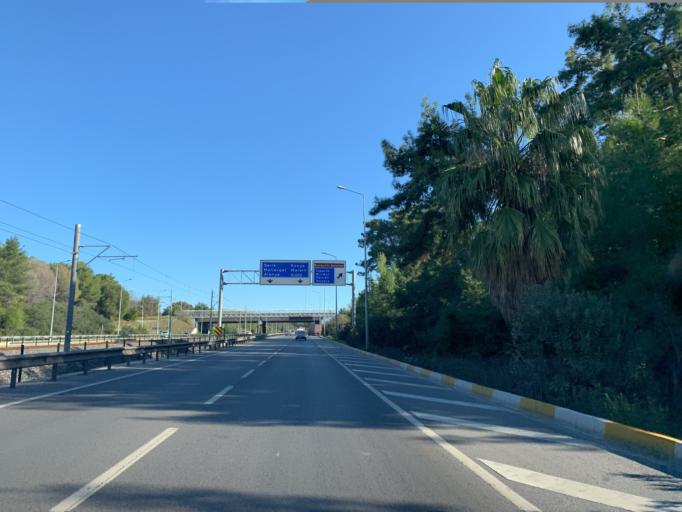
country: TR
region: Antalya
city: Aksu
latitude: 36.9438
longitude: 30.8289
